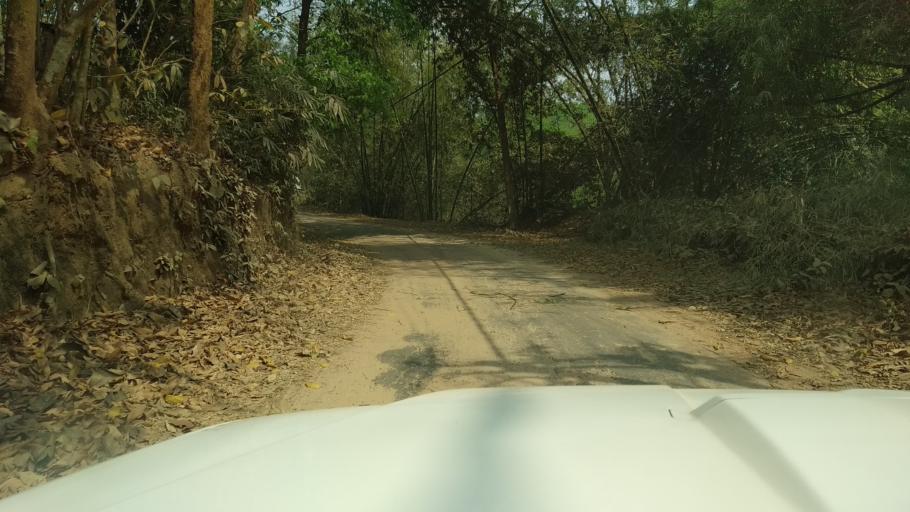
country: IN
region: Tripura
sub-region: West Tripura
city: Sonamura
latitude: 23.4229
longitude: 91.2916
